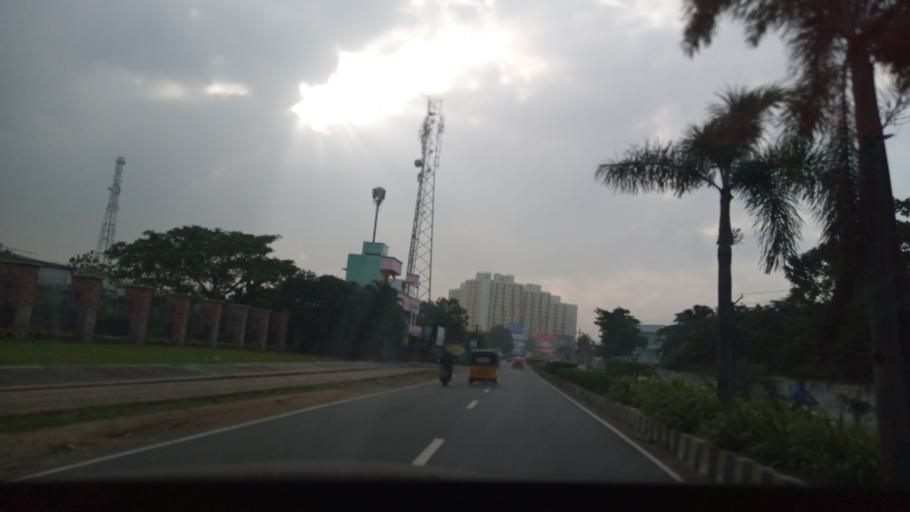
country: IN
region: Tamil Nadu
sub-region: Kancheepuram
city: Vengavasal
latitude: 12.8400
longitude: 80.1531
